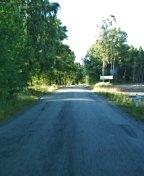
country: SE
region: Uppsala
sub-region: Habo Kommun
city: Balsta
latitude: 59.6908
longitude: 17.5336
